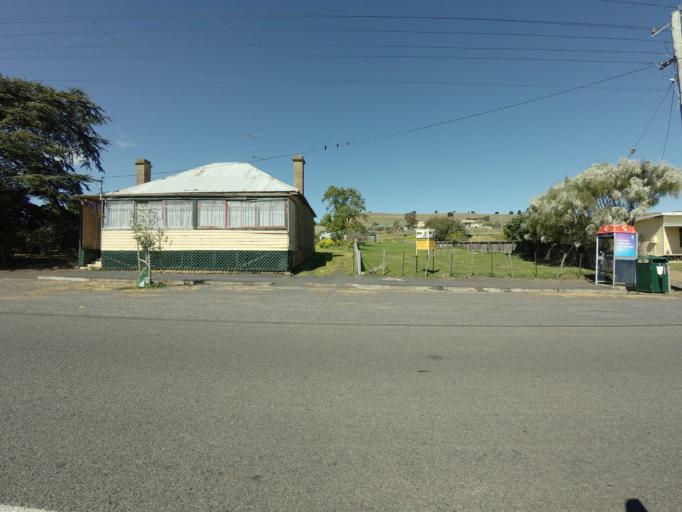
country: AU
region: Tasmania
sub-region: Derwent Valley
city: New Norfolk
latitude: -42.5559
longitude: 146.8343
